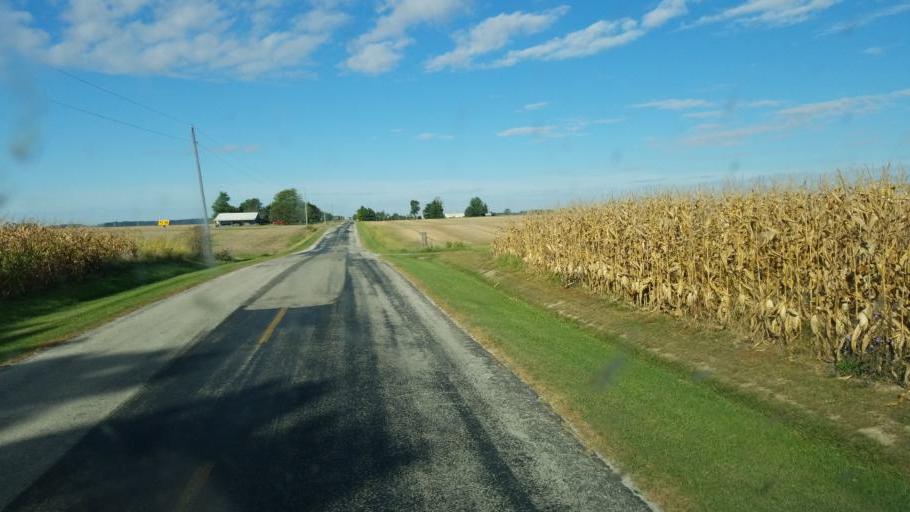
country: US
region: Ohio
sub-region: Marion County
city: Marion
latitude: 40.6885
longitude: -83.0426
